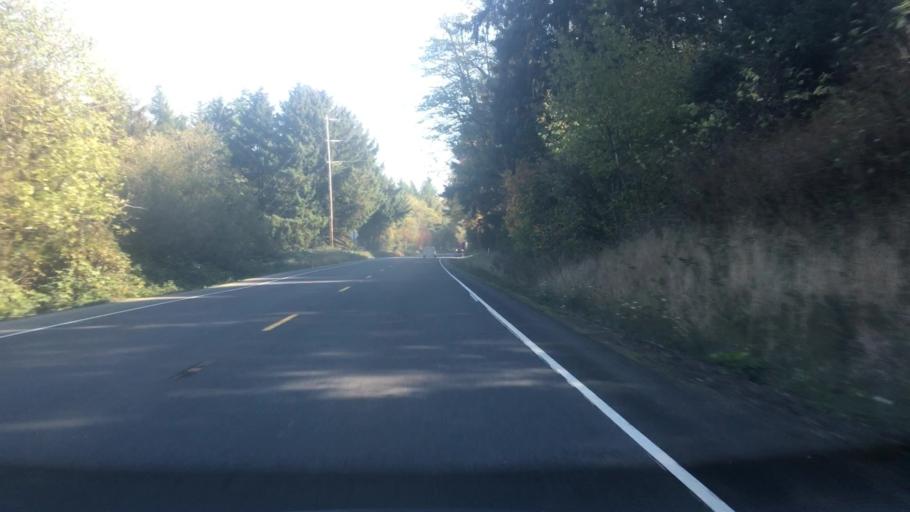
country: US
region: Oregon
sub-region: Lincoln County
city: Rose Lodge
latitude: 45.0125
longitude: -123.9282
